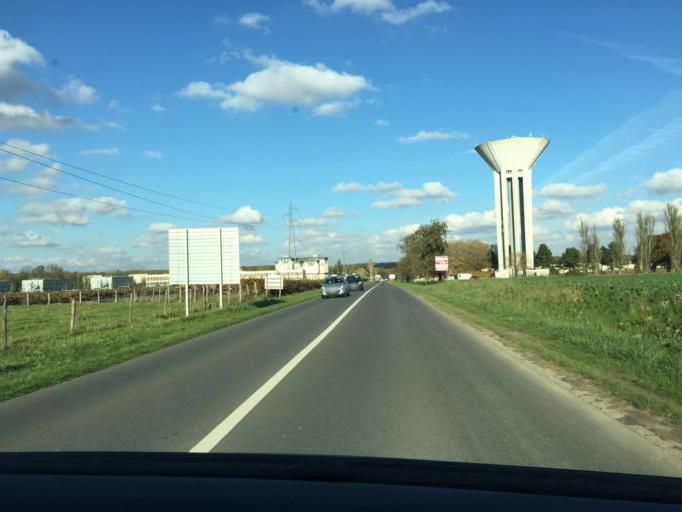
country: FR
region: Ile-de-France
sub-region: Departement des Yvelines
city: Jouy-en-Josas
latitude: 48.7512
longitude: 2.1672
